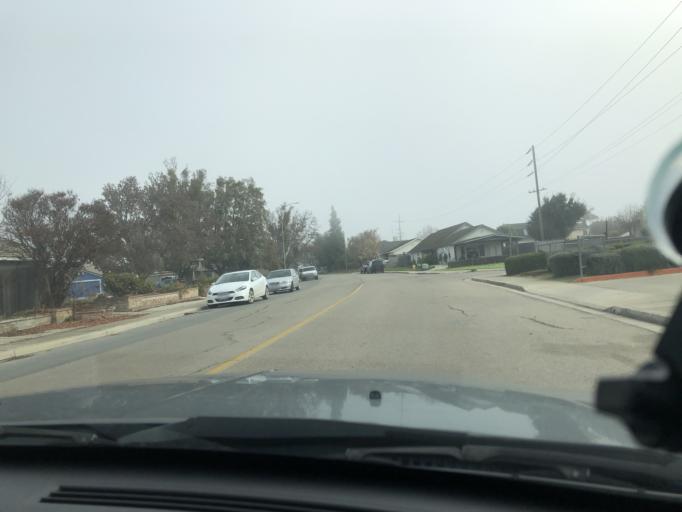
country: US
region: California
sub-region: Monterey County
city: King City
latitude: 36.2118
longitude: -121.1372
